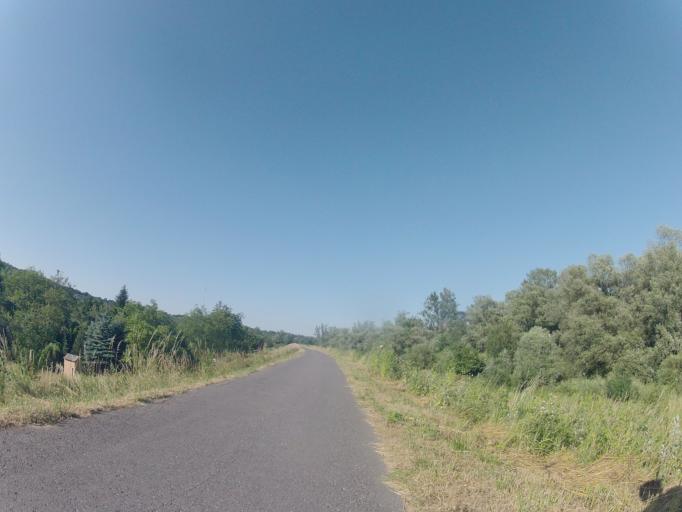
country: PL
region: Lesser Poland Voivodeship
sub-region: Krakow
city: Krakow
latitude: 50.0415
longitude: 19.8964
